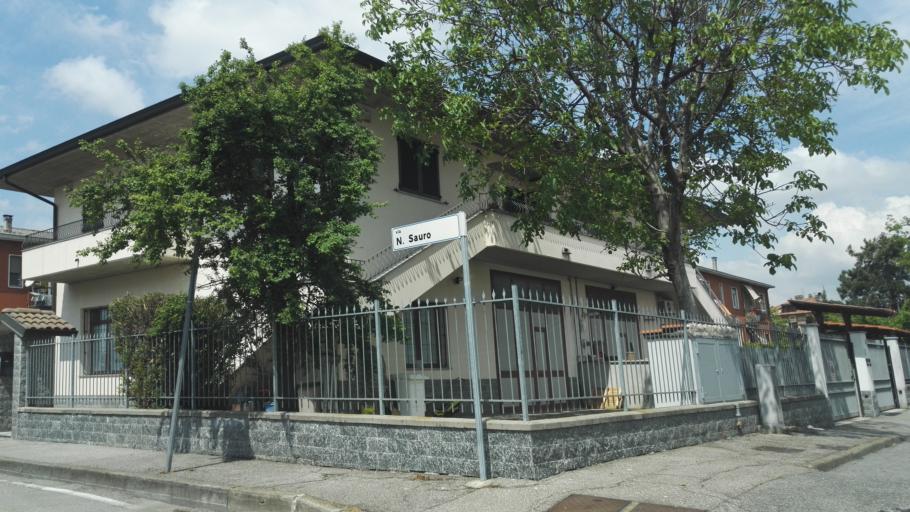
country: IT
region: Lombardy
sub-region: Citta metropolitana di Milano
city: Mezzate
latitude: 45.4382
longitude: 9.2874
